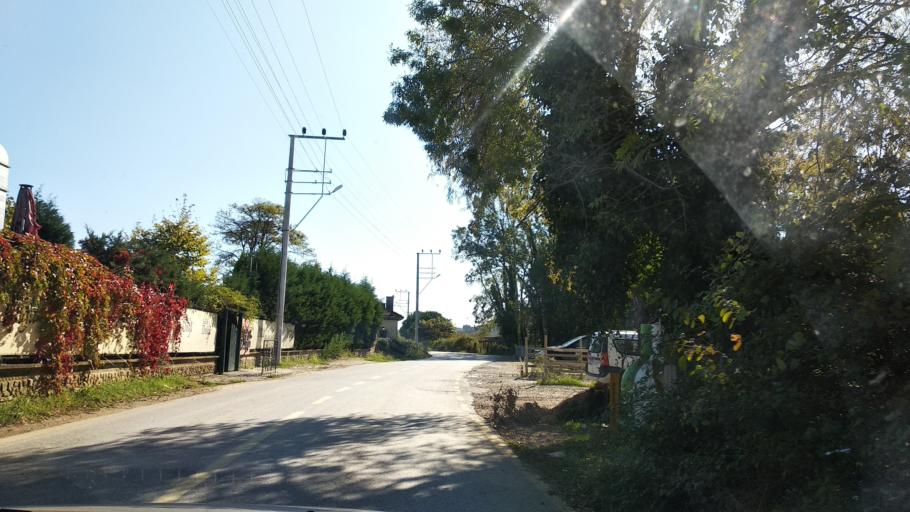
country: TR
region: Sakarya
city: Karasu
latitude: 41.1159
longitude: 30.6443
